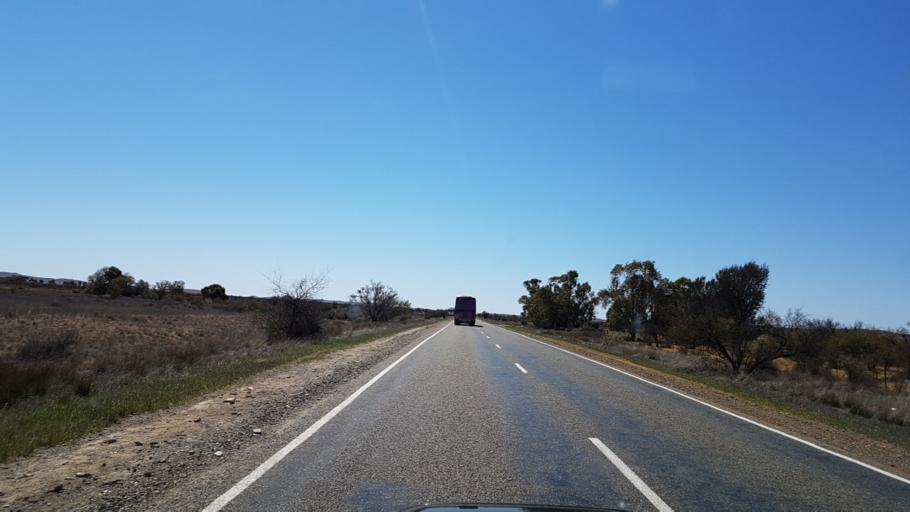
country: AU
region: South Australia
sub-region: Peterborough
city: Peterborough
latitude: -33.1426
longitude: 138.9297
